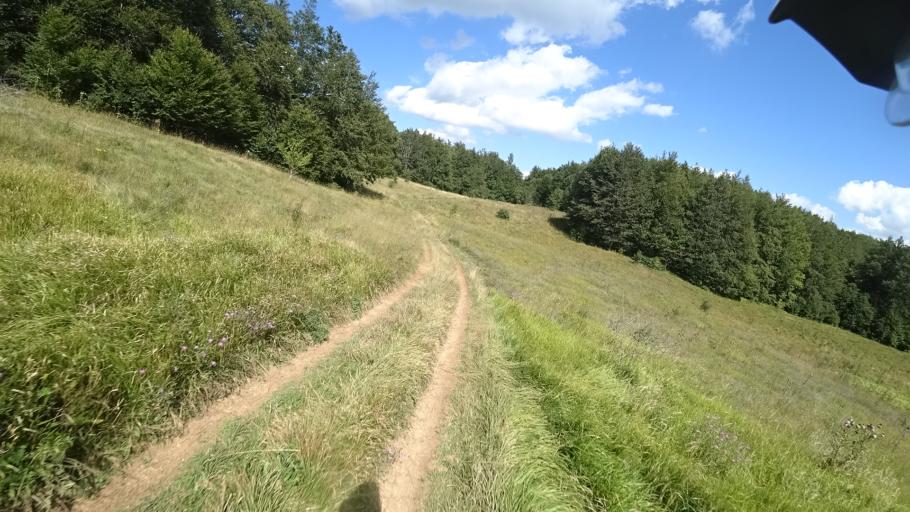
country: HR
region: Zadarska
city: Gracac
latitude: 44.4303
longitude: 15.9958
